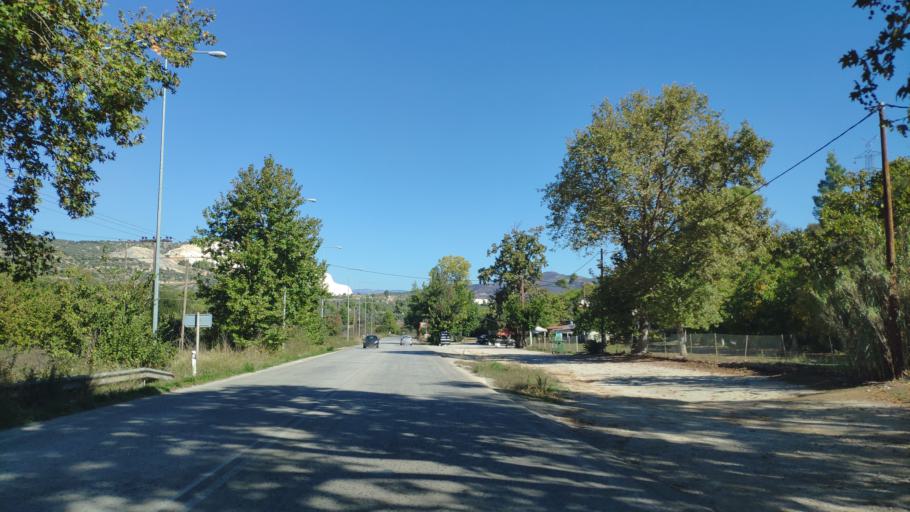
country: GR
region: Peloponnese
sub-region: Nomos Korinthias
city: Khiliomodhi
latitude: 37.8273
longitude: 22.8854
